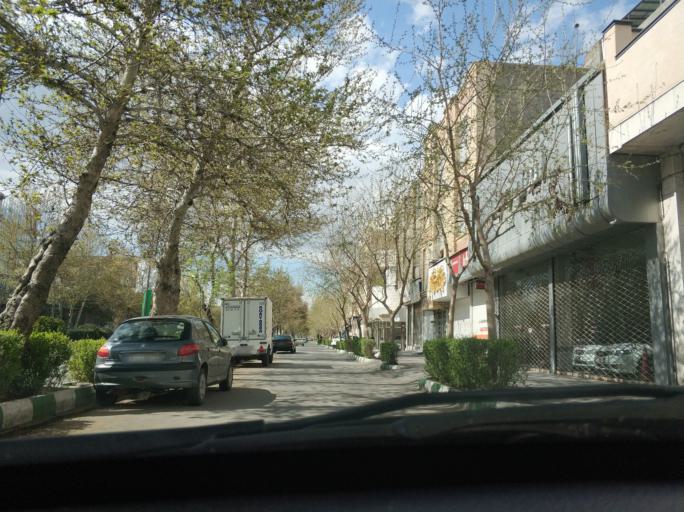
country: IR
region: Razavi Khorasan
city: Mashhad
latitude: 36.2705
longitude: 59.5965
